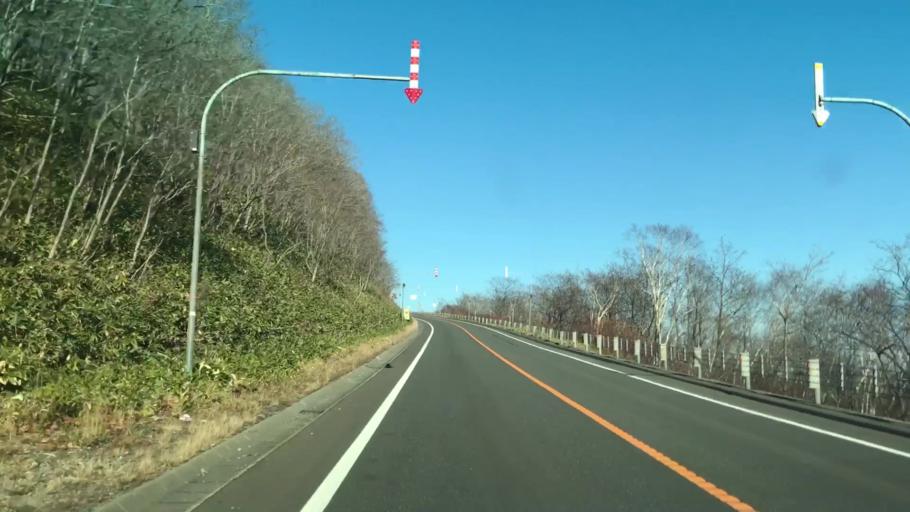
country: JP
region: Hokkaido
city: Otofuke
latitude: 42.9662
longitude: 142.7949
